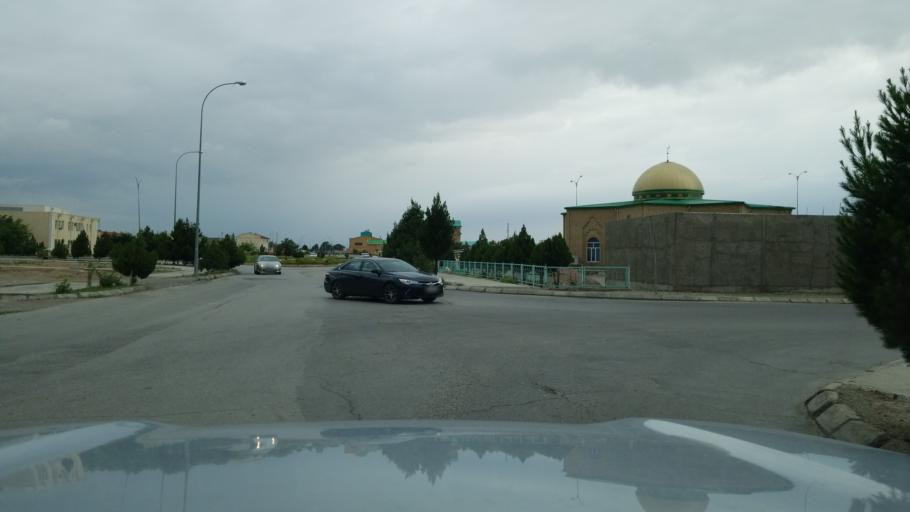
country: TM
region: Balkan
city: Serdar
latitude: 38.9772
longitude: 56.2791
